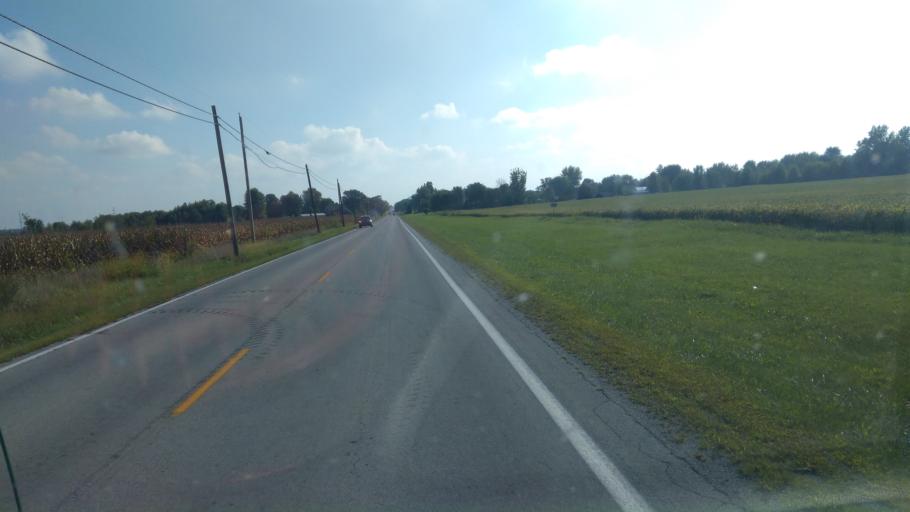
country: US
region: Ohio
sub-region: Hardin County
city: Forest
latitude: 40.7859
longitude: -83.5225
